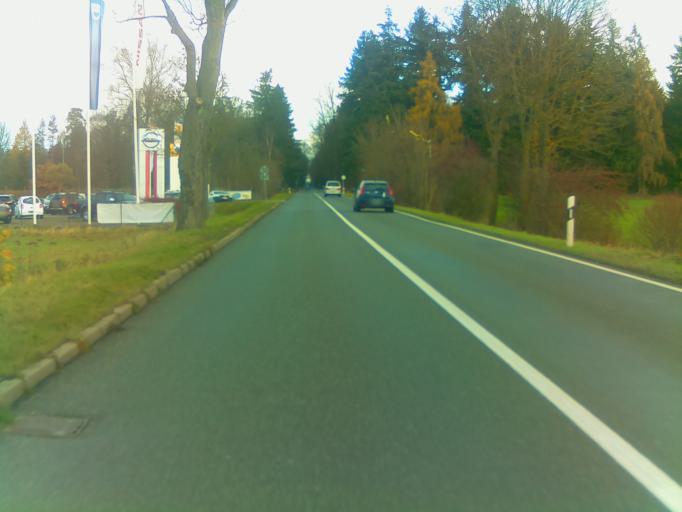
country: DE
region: Thuringia
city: Hildburghausen
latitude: 50.4422
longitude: 10.7347
